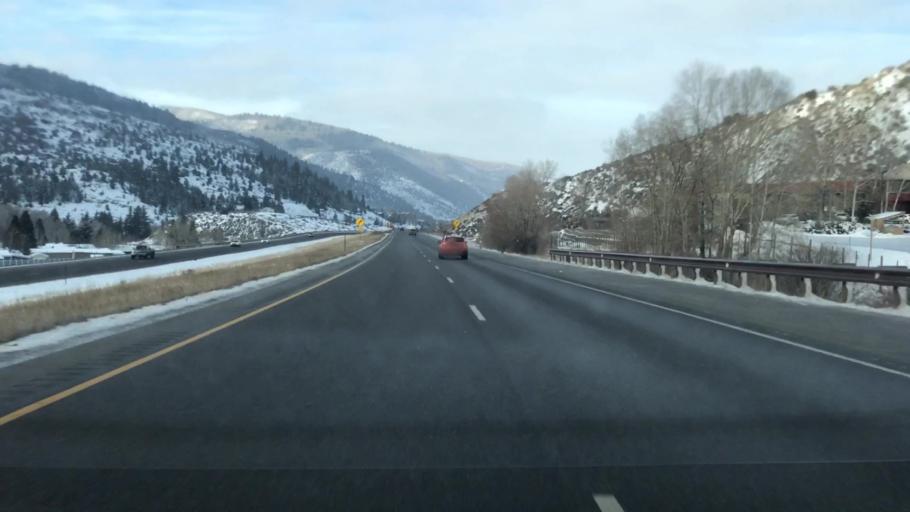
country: US
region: Colorado
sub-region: Eagle County
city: Avon
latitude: 39.6397
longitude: -106.5379
